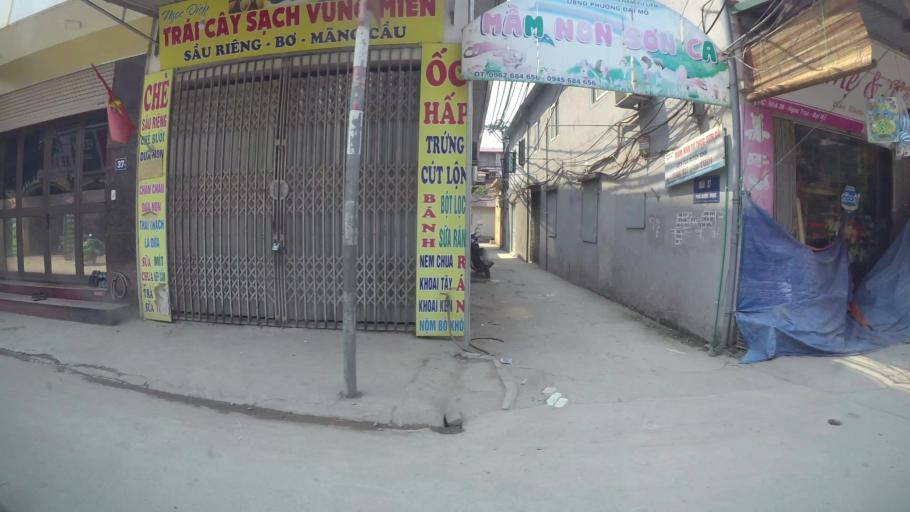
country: VN
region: Ha Noi
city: Ha Dong
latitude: 20.9891
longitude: 105.7725
